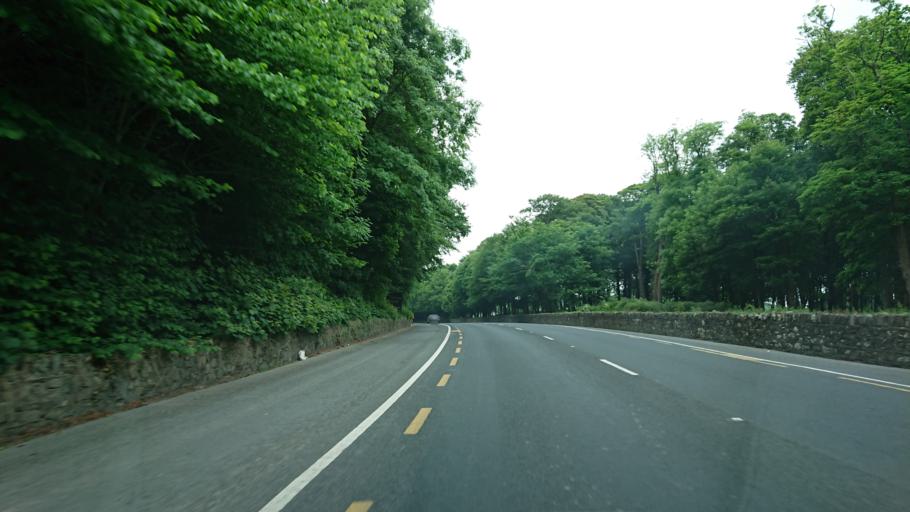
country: IE
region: Munster
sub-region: Waterford
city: Waterford
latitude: 52.2088
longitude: -7.1162
